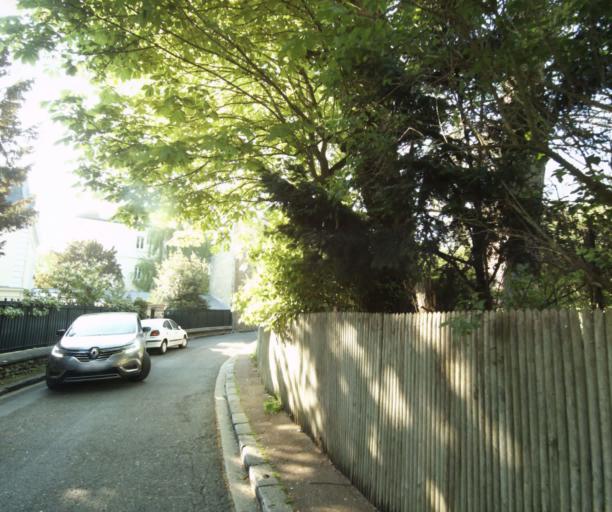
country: FR
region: Ile-de-France
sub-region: Departement des Hauts-de-Seine
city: Ville-d'Avray
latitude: 48.8280
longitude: 2.2029
